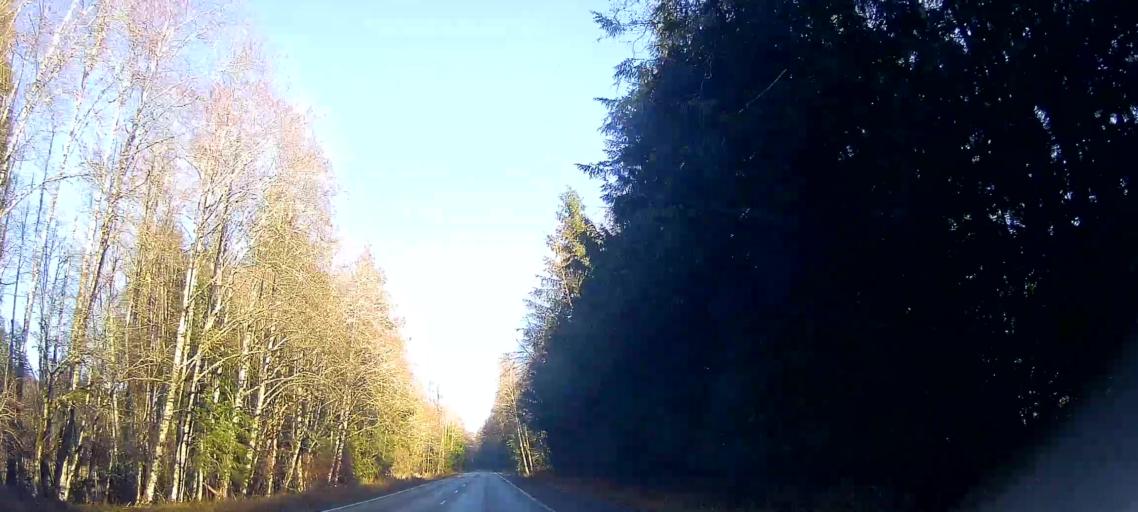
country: US
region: Washington
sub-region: Snohomish County
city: Darrington
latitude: 48.6034
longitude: -121.7618
